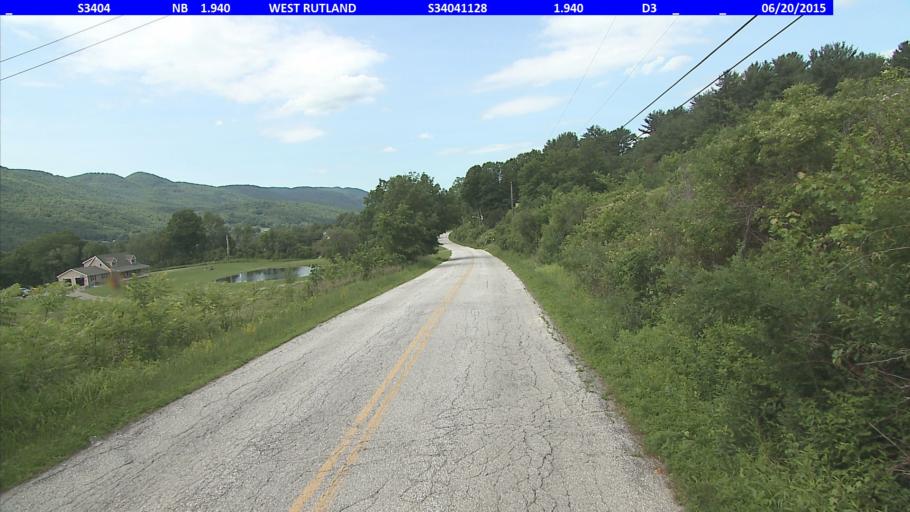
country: US
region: Vermont
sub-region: Rutland County
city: West Rutland
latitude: 43.6189
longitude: -73.0522
